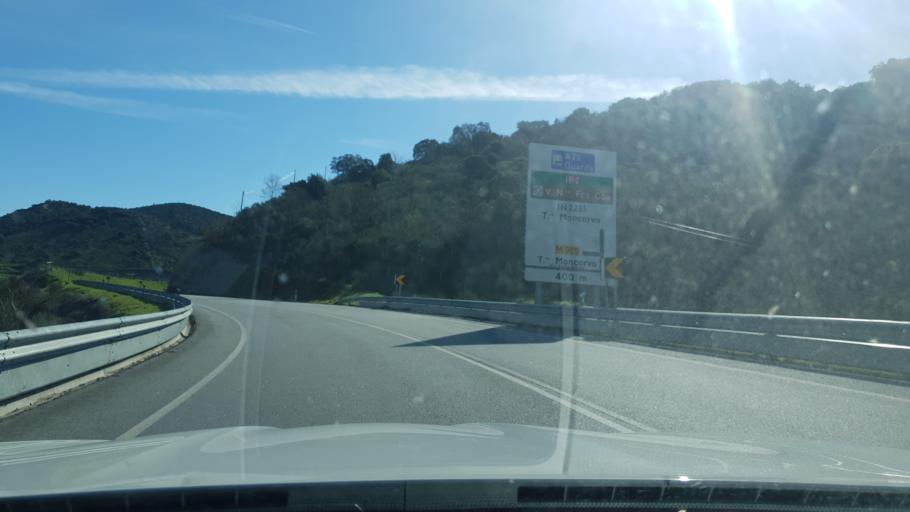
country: PT
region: Braganca
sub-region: Torre de Moncorvo
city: Torre de Moncorvo
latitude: 41.2122
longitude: -7.0880
